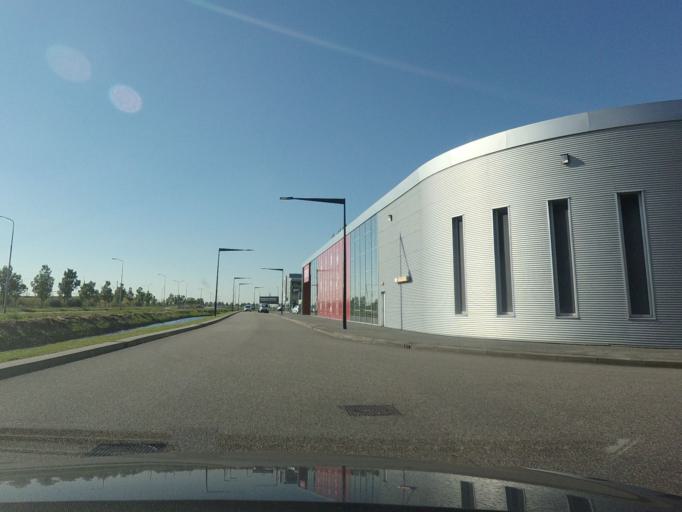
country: NL
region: North Holland
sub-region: Gemeente Haarlemmermeer
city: Hoofddorp
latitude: 52.2868
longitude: 4.6833
